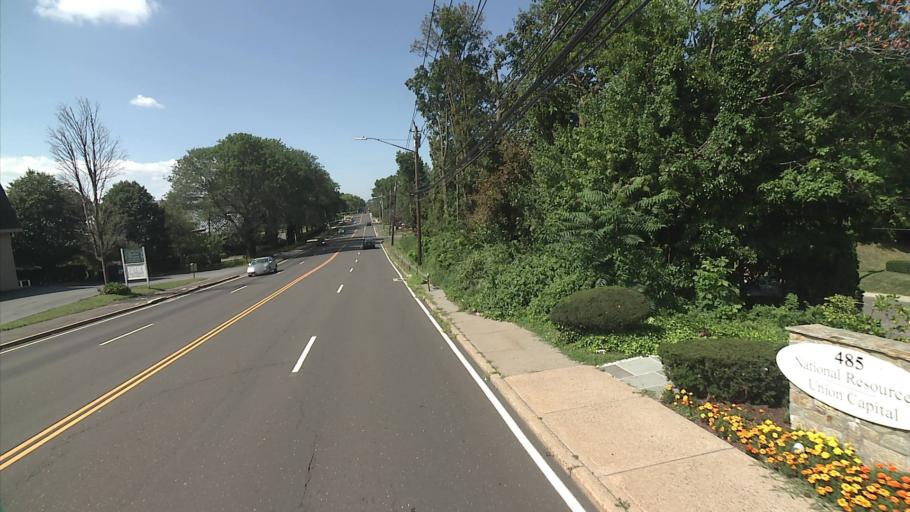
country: US
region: Connecticut
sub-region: Fairfield County
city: Greenwich
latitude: 41.0196
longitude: -73.6438
